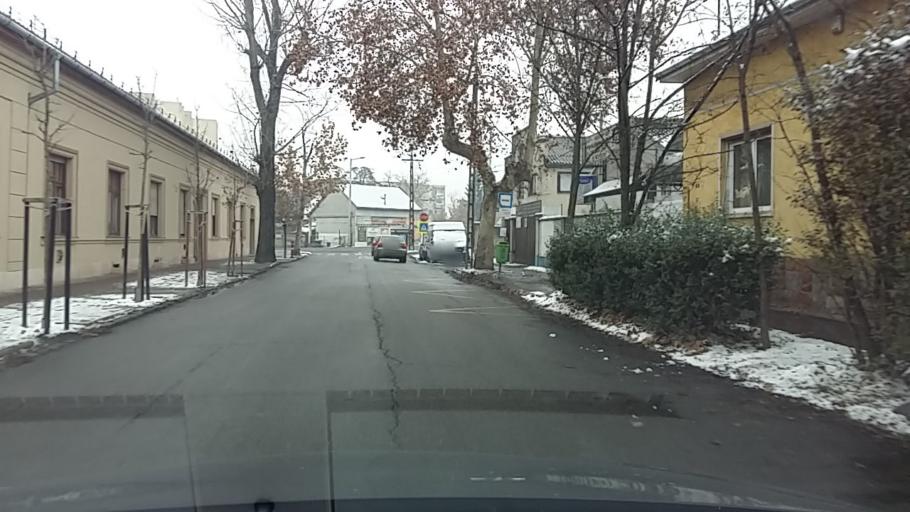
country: HU
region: Budapest
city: Budapest XV. keruelet
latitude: 47.5618
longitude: 19.1076
